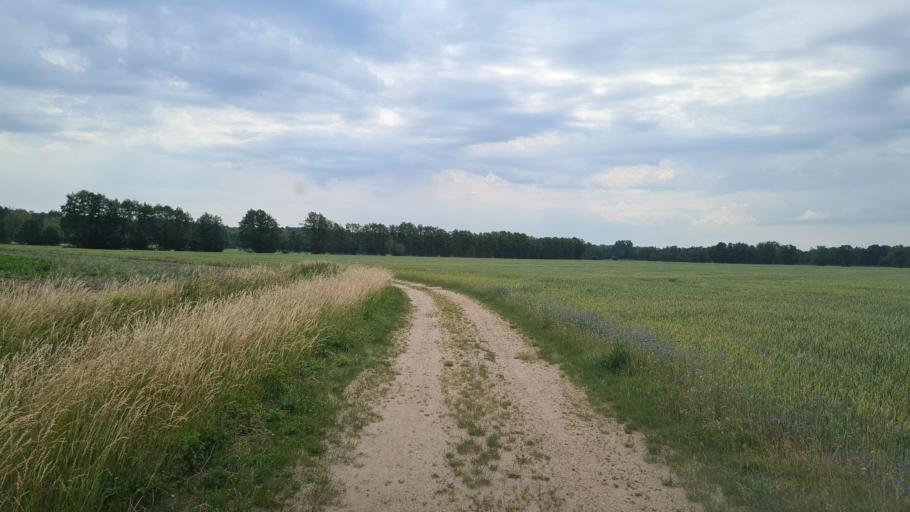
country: DE
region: Brandenburg
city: Finsterwalde
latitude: 51.6824
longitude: 13.7326
